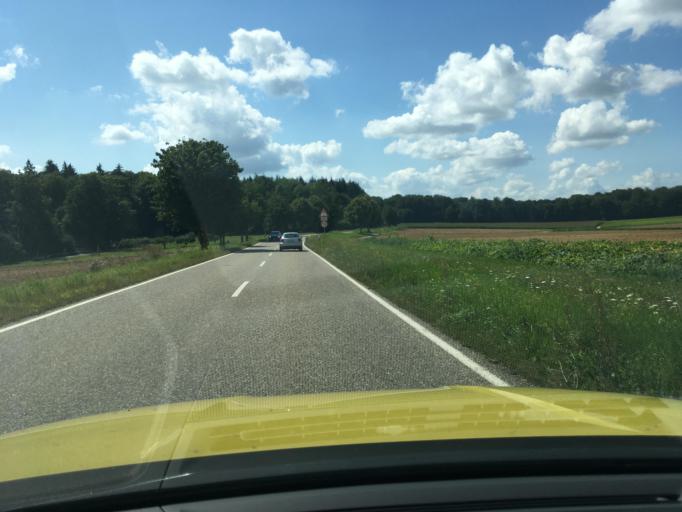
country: DE
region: Baden-Wuerttemberg
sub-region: Regierungsbezirk Stuttgart
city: Massenbachhausen
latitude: 49.1717
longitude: 9.0244
